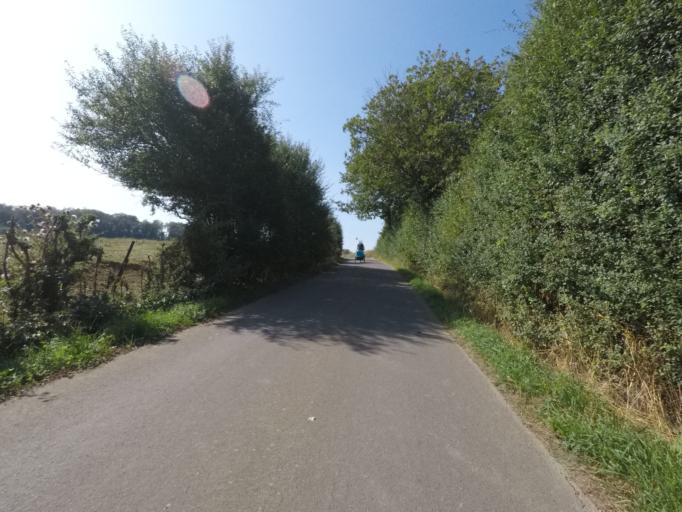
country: LU
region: Luxembourg
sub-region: Canton de Capellen
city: Mamer
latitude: 49.6477
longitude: 6.0207
